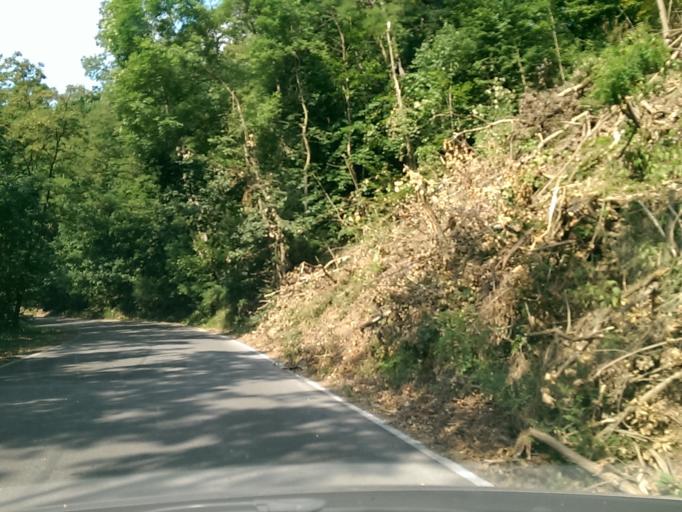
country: CZ
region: Central Bohemia
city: Knezmost
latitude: 50.5002
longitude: 15.0544
